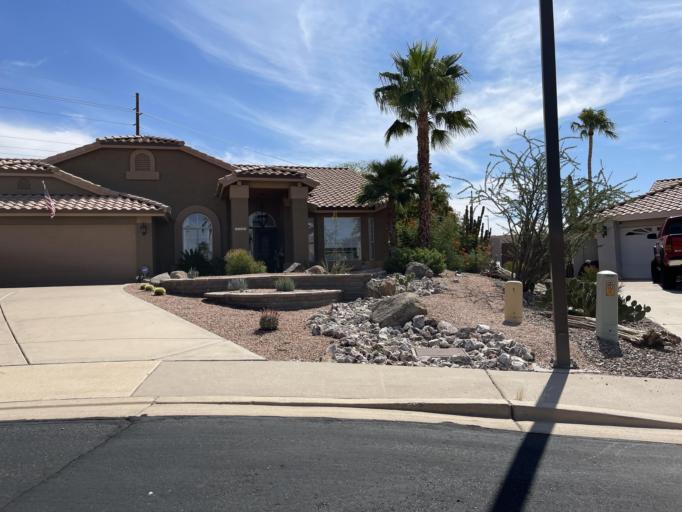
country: US
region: Arizona
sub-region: Maricopa County
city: Fountain Hills
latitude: 33.4907
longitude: -111.6847
